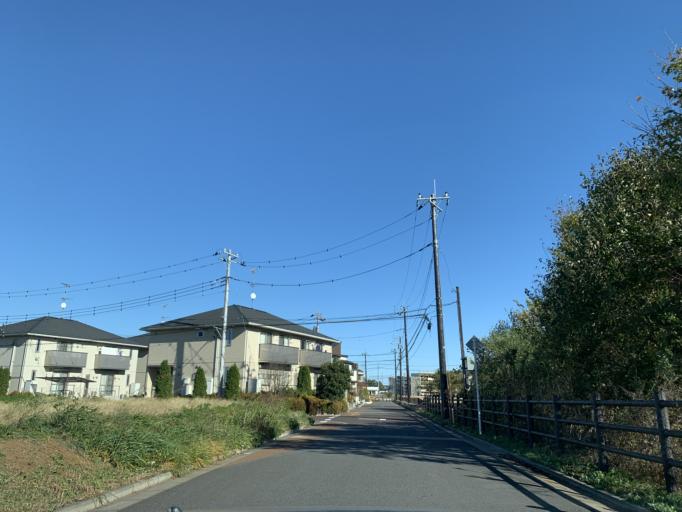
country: JP
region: Chiba
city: Kashiwa
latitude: 35.8996
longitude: 139.9474
